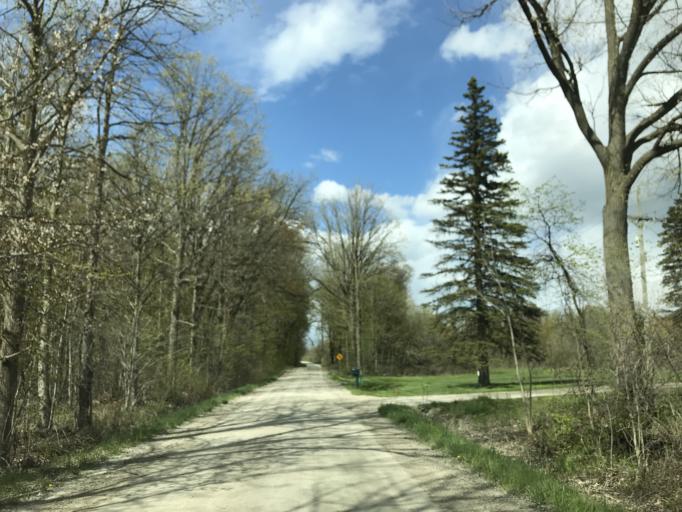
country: US
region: Michigan
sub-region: Oakland County
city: South Lyon
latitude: 42.3785
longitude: -83.6262
